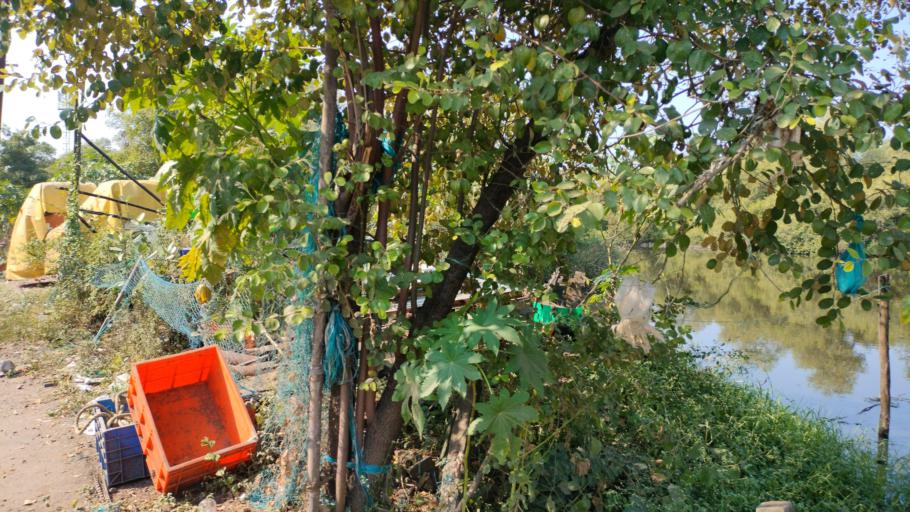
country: IN
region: Maharashtra
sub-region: Thane
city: Bhayandar
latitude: 19.3295
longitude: 72.8070
